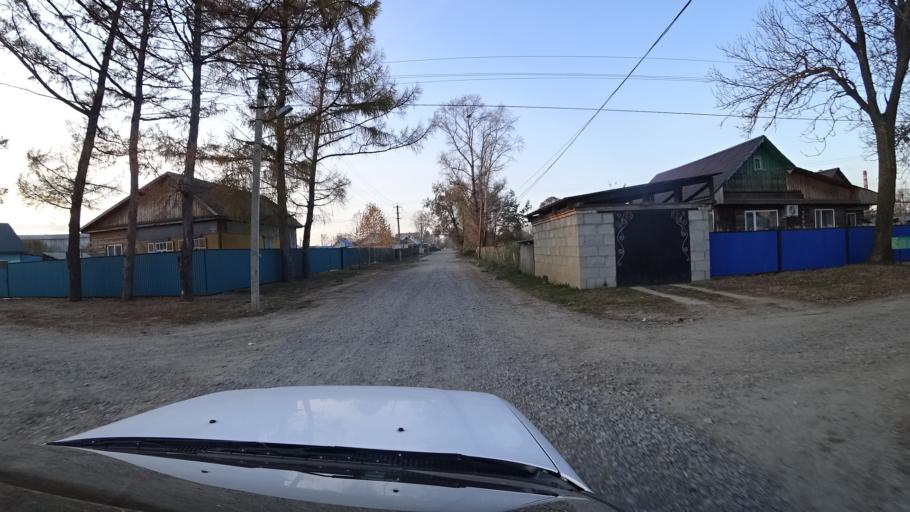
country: RU
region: Primorskiy
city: Dal'nerechensk
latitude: 45.9459
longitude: 133.8218
